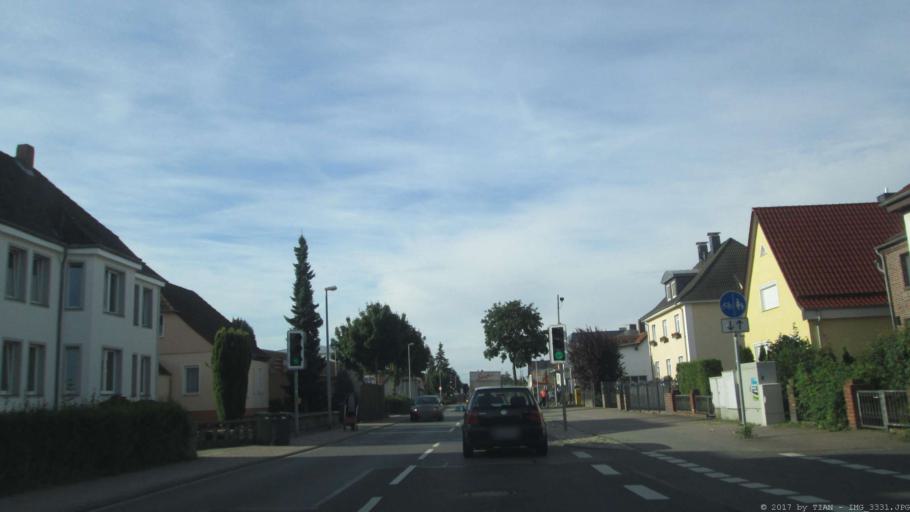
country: DE
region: Lower Saxony
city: Ruhen
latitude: 52.4333
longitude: 10.8477
